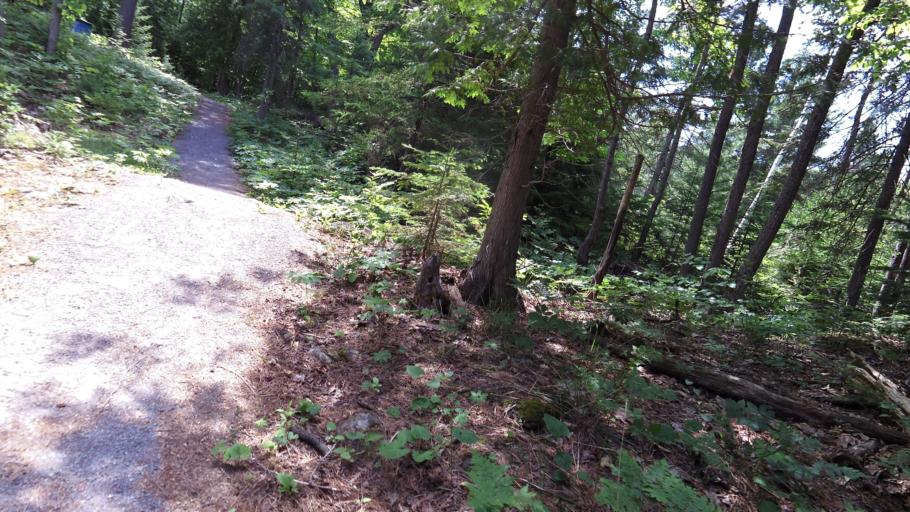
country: CA
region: Ontario
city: Arnprior
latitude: 45.4600
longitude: -76.2617
